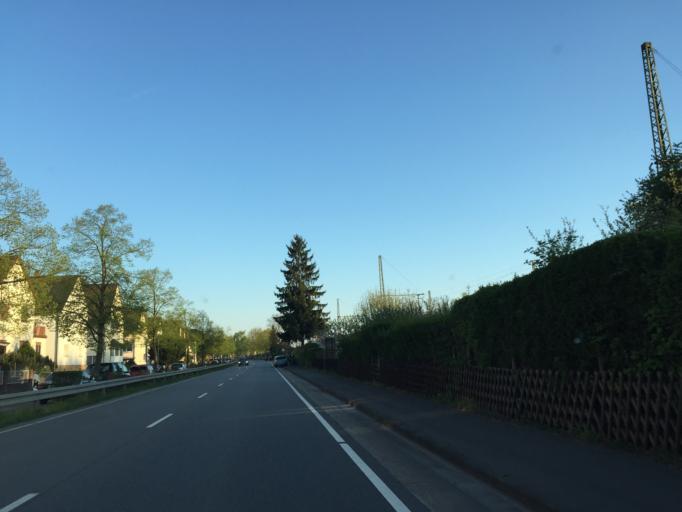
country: DE
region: Hesse
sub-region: Regierungsbezirk Darmstadt
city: Bensheim
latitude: 49.6735
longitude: 8.6197
